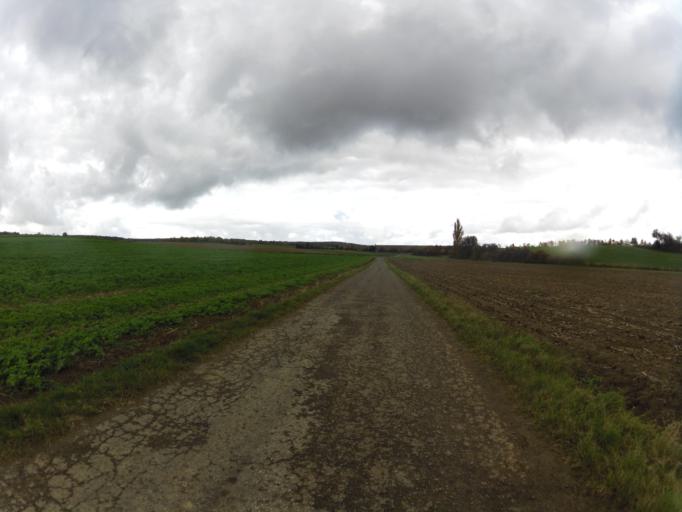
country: DE
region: Bavaria
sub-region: Regierungsbezirk Unterfranken
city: Kurnach
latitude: 49.8698
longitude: 10.0115
